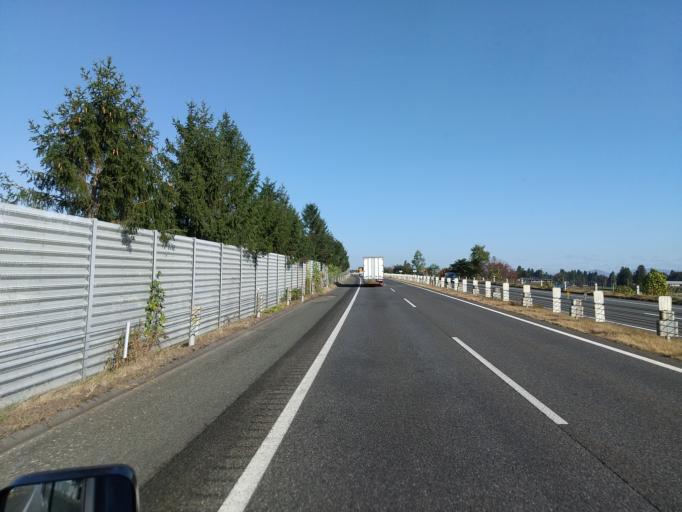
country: JP
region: Iwate
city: Hanamaki
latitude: 39.4784
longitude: 141.1103
